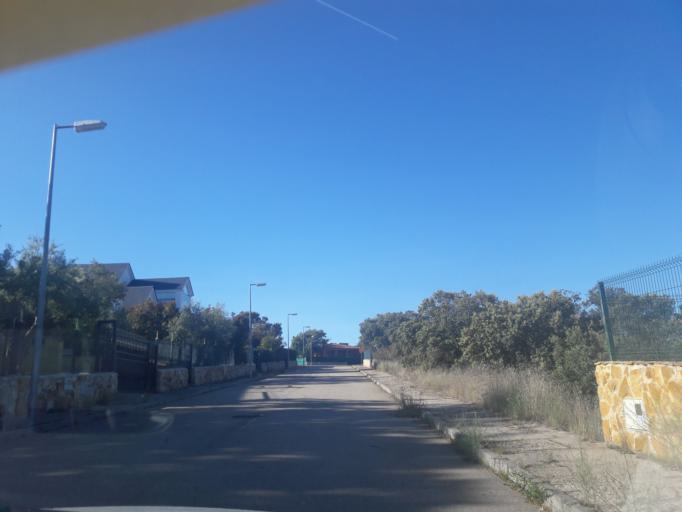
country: ES
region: Castille and Leon
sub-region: Provincia de Salamanca
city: Martinamor
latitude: 40.8105
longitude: -5.6422
